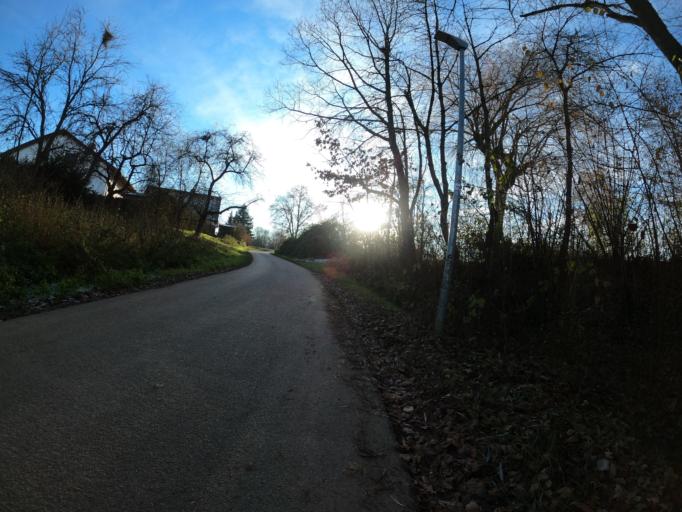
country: DE
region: Baden-Wuerttemberg
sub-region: Regierungsbezirk Stuttgart
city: Boll
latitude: 48.6637
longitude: 9.6112
